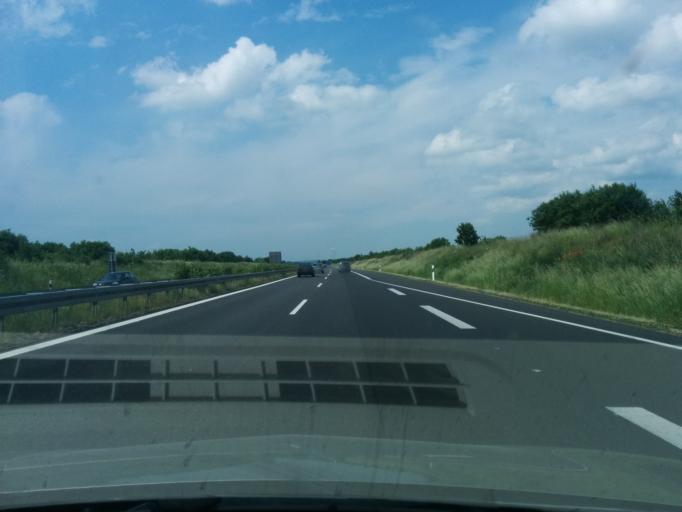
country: DE
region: Brandenburg
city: Goritz
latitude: 53.4986
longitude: 13.9077
